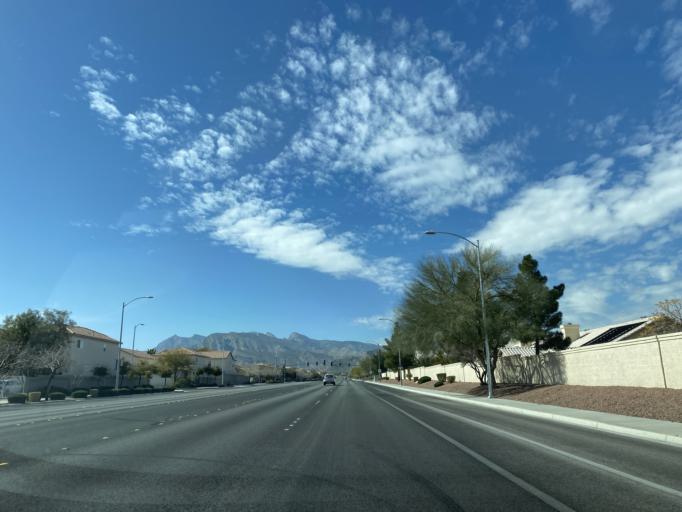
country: US
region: Nevada
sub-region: Clark County
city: Spring Valley
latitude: 36.2334
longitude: -115.2674
